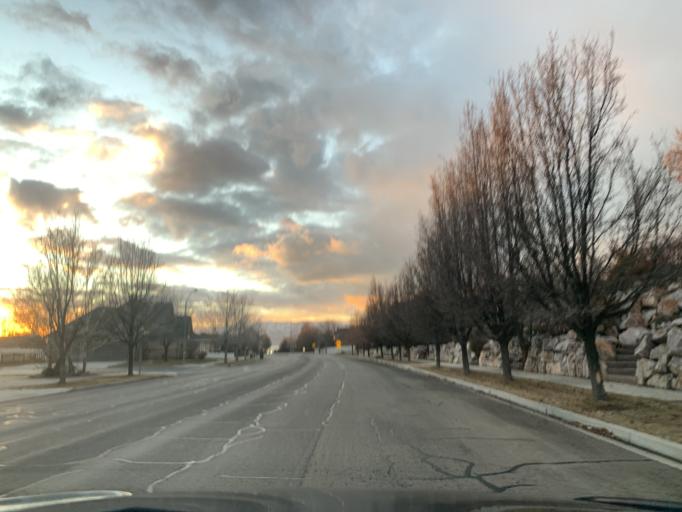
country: US
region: Utah
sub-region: Utah County
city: Provo
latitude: 40.2570
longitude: -111.6873
